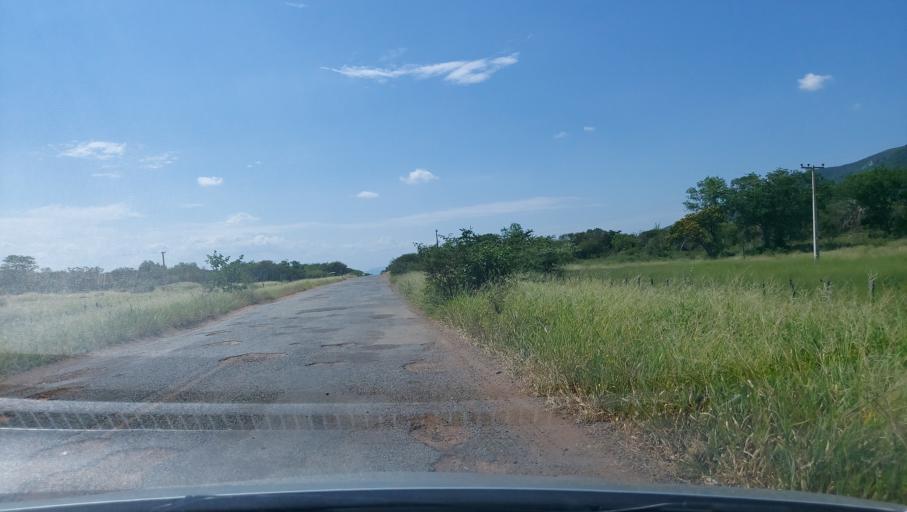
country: BR
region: Bahia
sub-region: Oliveira Dos Brejinhos
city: Beira Rio
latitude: -12.1626
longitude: -42.5490
